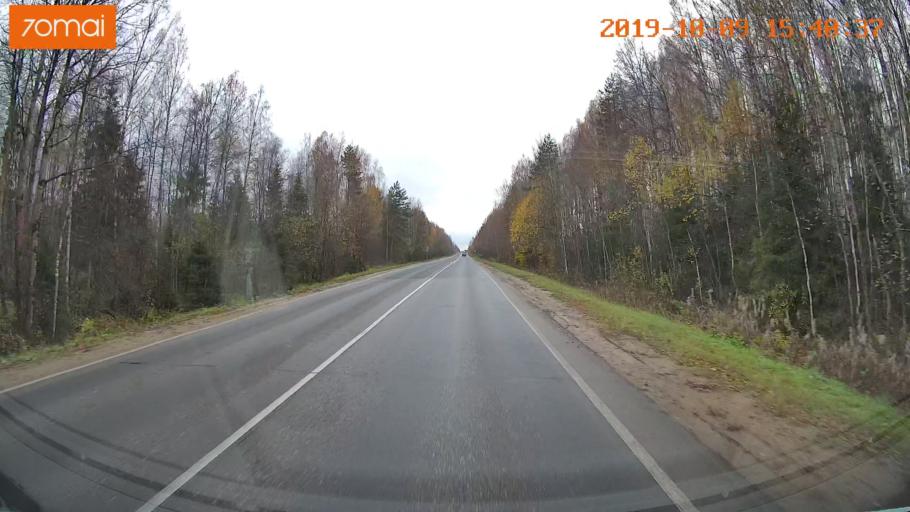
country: RU
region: Kostroma
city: Oktyabr'skiy
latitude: 57.8859
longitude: 41.1409
